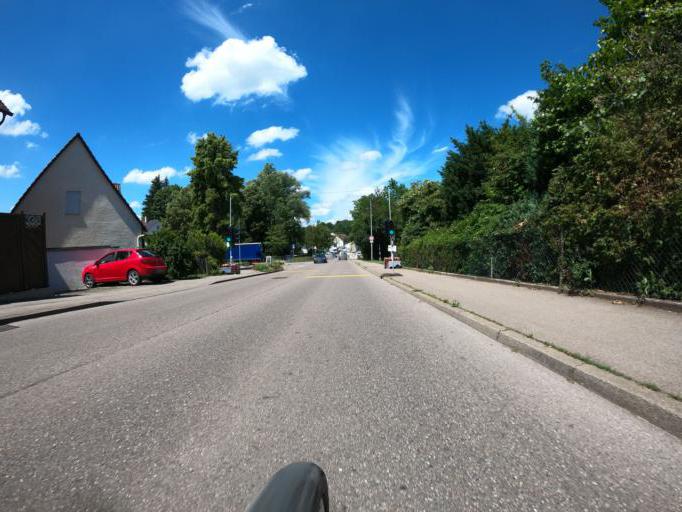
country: DE
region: Baden-Wuerttemberg
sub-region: Regierungsbezirk Stuttgart
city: Sersheim
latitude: 48.9628
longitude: 9.0575
